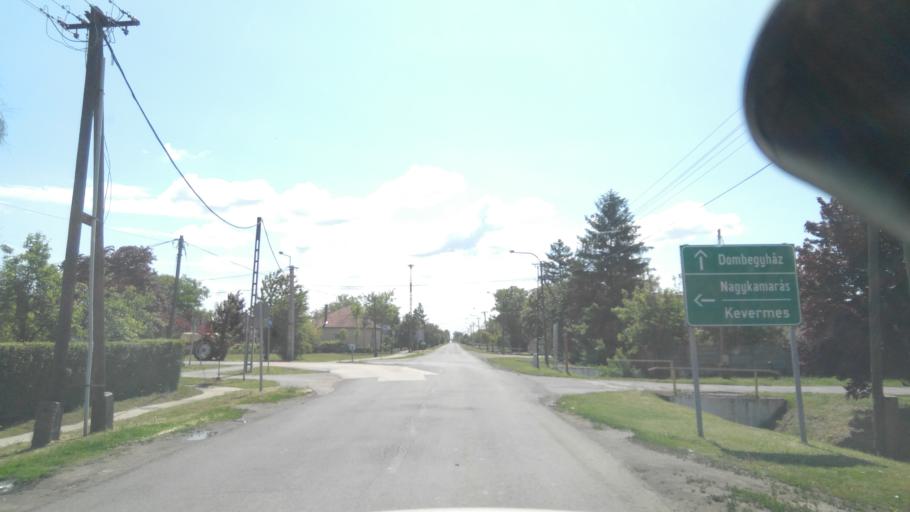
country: HU
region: Bekes
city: Kunagota
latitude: 46.4191
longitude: 21.0344
